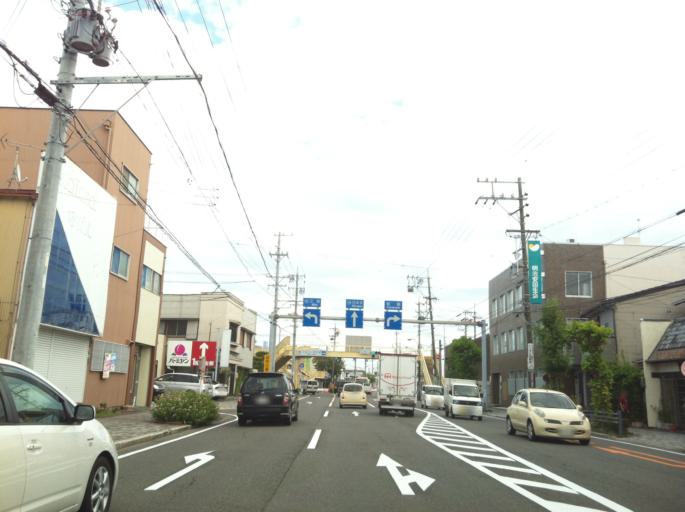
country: JP
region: Shizuoka
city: Shizuoka-shi
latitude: 35.0100
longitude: 138.4801
